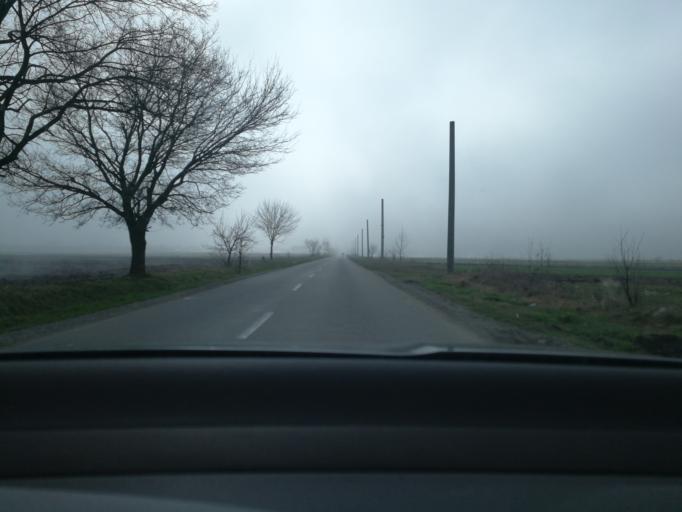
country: RO
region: Prahova
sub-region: Comuna Magureni
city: Lunca Prahovei
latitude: 45.0306
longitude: 25.7680
